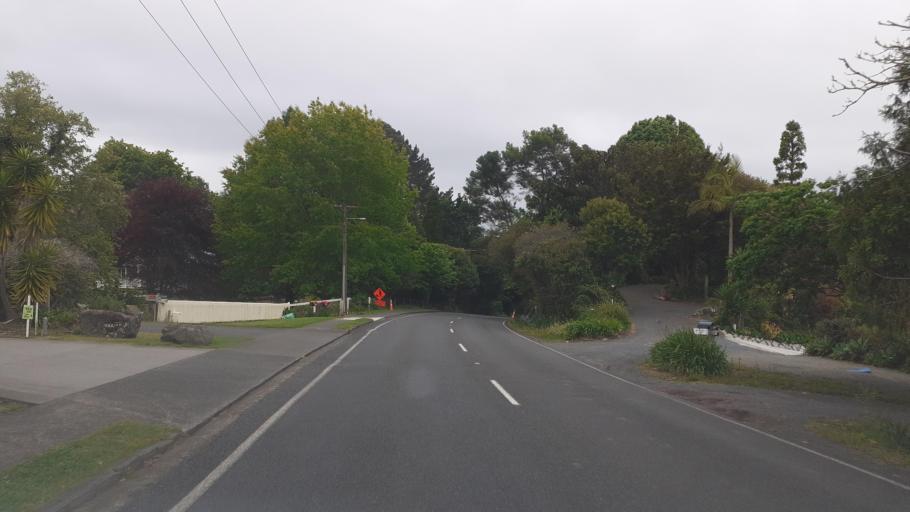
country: NZ
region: Northland
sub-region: Far North District
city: Kerikeri
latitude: -35.2046
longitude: 173.9663
